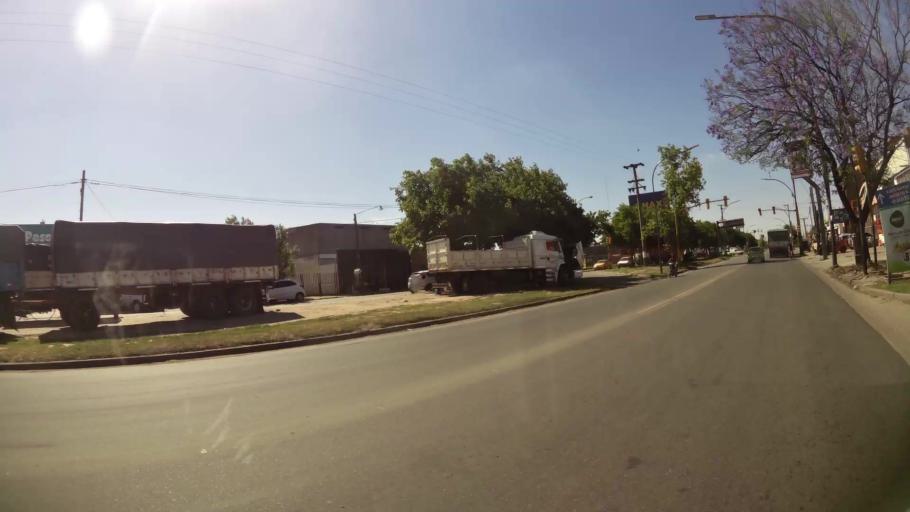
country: AR
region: Cordoba
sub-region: Departamento de Capital
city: Cordoba
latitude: -31.3692
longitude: -64.1761
